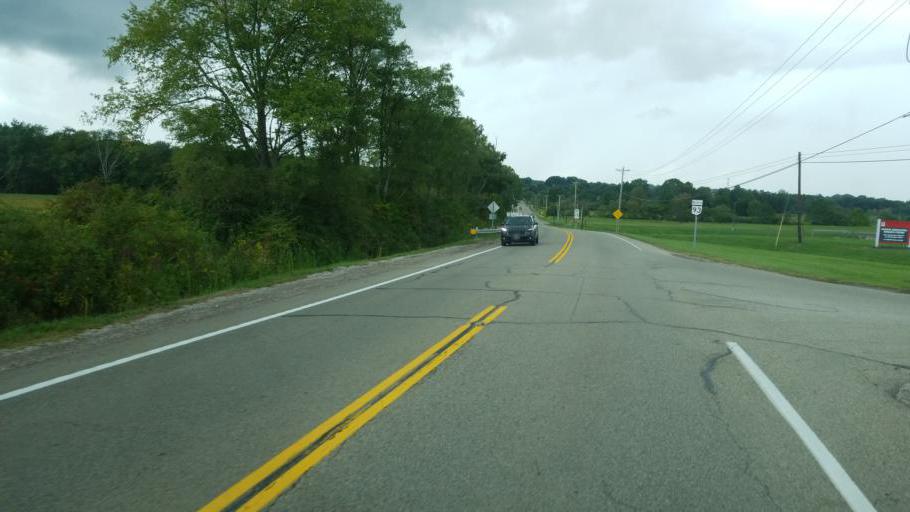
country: US
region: Ohio
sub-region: Jackson County
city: Jackson
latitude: 39.0202
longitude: -82.6080
